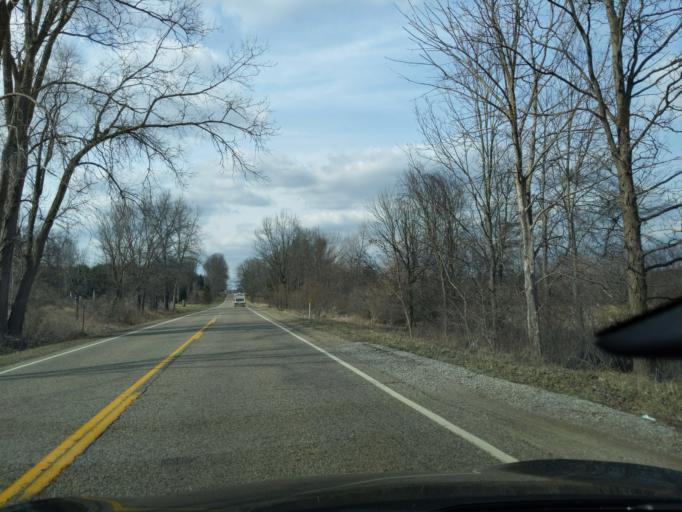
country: US
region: Michigan
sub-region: Jackson County
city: Jackson
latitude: 42.3442
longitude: -84.4142
